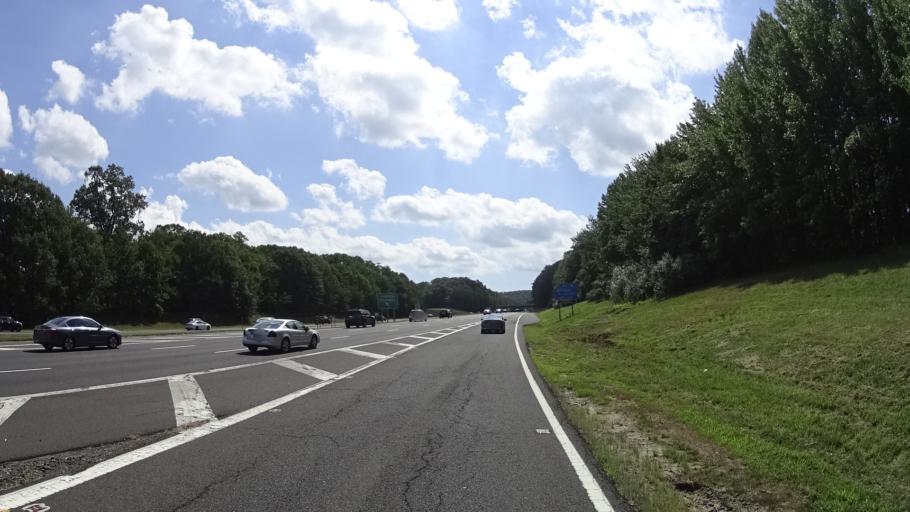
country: US
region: New Jersey
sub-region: Monmouth County
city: Strathmore
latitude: 40.4031
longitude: -74.1951
